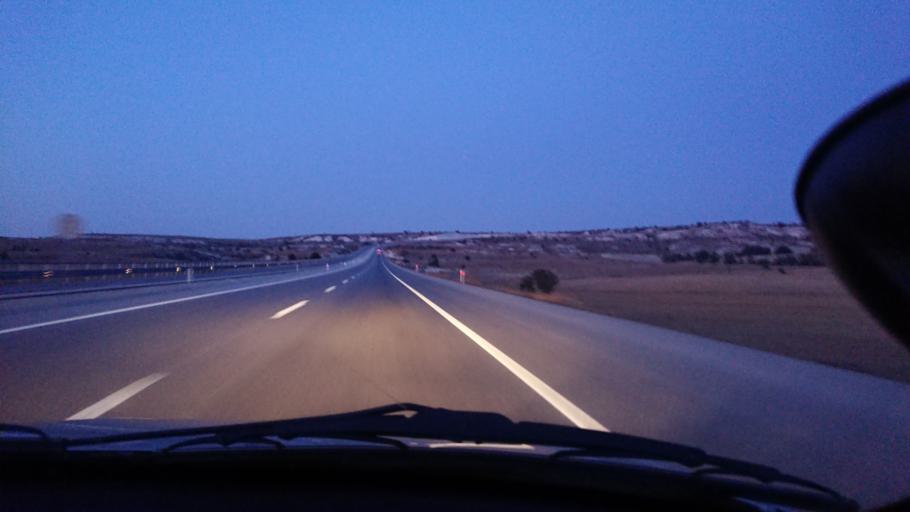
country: TR
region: Kuetahya
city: Cavdarhisar
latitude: 39.1338
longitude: 29.5540
